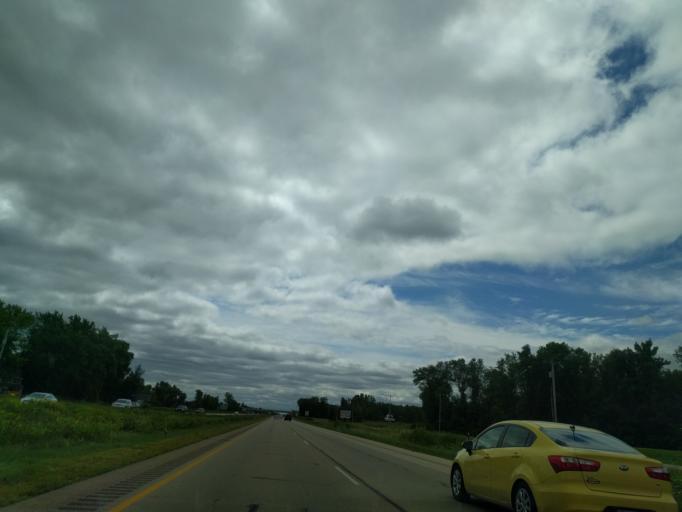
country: US
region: Wisconsin
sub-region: Brown County
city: Suamico
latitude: 44.7580
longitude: -88.0512
